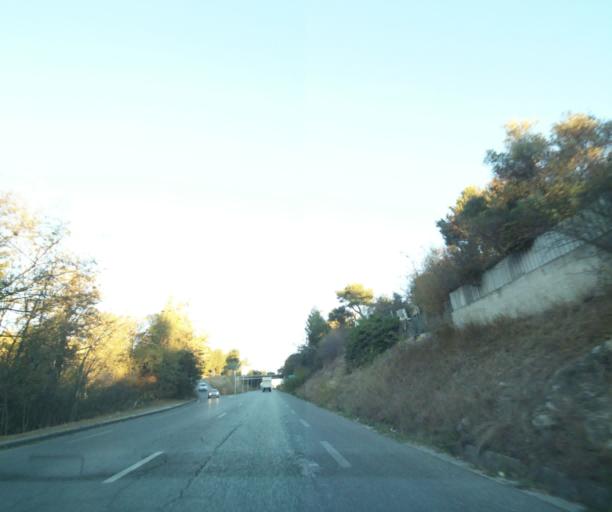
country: FR
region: Provence-Alpes-Cote d'Azur
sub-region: Departement des Bouches-du-Rhone
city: Allauch
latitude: 43.3103
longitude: 5.4659
